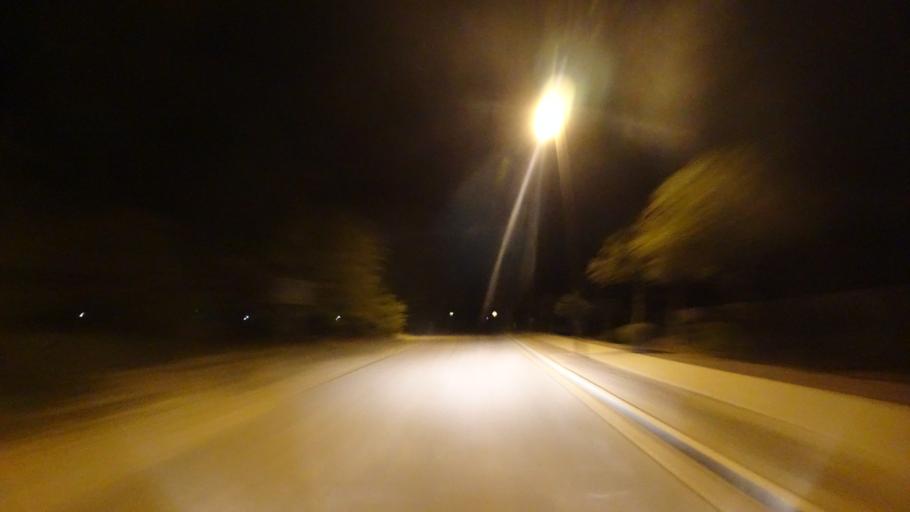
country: US
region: Arizona
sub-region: Maricopa County
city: Queen Creek
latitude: 33.2144
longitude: -111.7033
